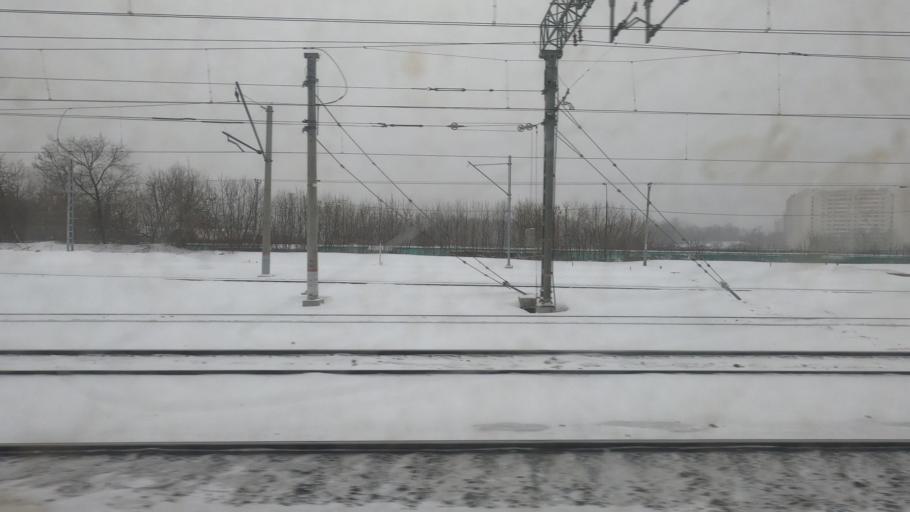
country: RU
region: Moscow
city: Ryazanskiy
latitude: 55.7357
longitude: 37.7750
